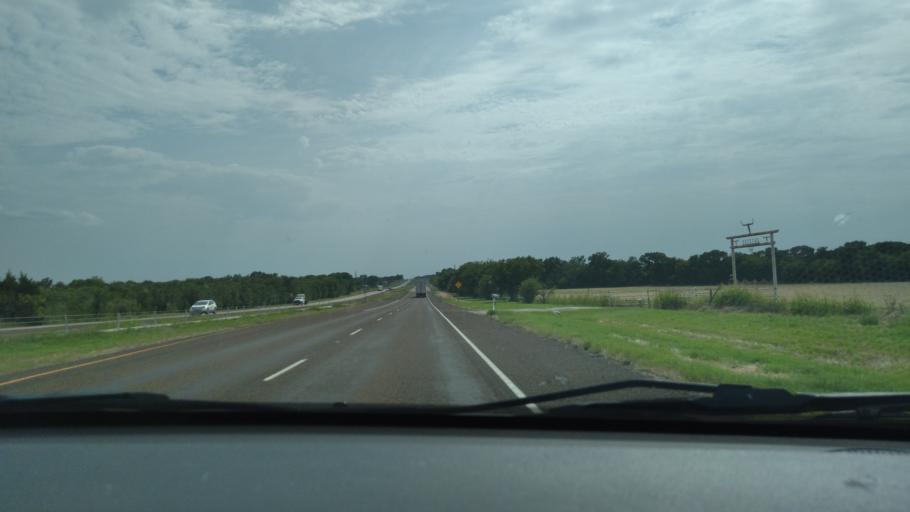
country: US
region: Texas
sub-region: Navarro County
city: Corsicana
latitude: 32.0329
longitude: -96.5567
